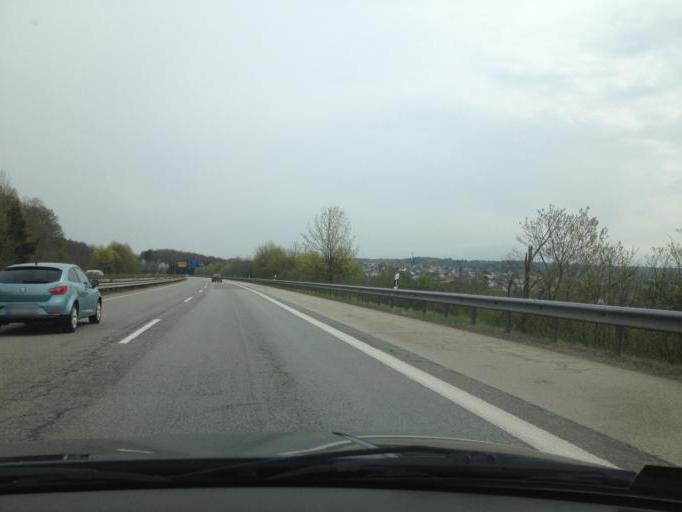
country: DE
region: Rheinland-Pfalz
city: Rieschweiler-Muhlbach
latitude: 49.2137
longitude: 7.5163
